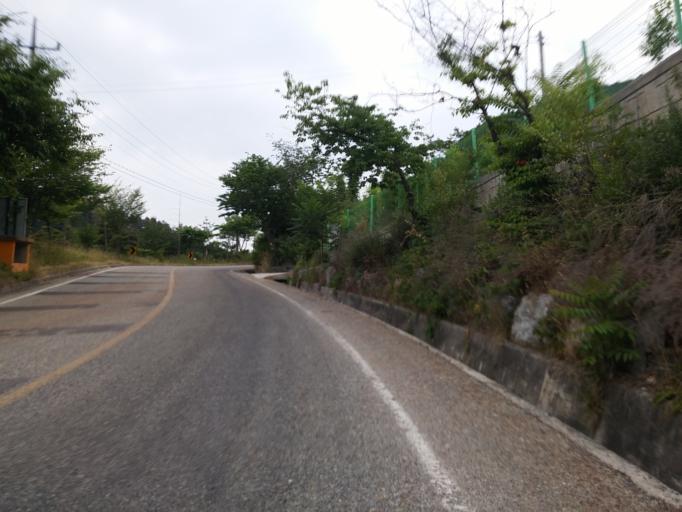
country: KR
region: Chungcheongnam-do
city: Kinzan
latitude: 36.1873
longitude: 127.5443
